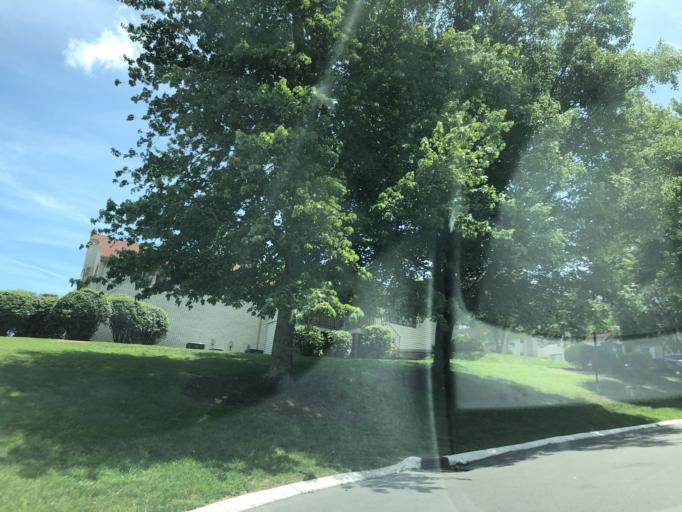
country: US
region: Tennessee
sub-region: Rutherford County
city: La Vergne
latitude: 36.0398
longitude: -86.6619
